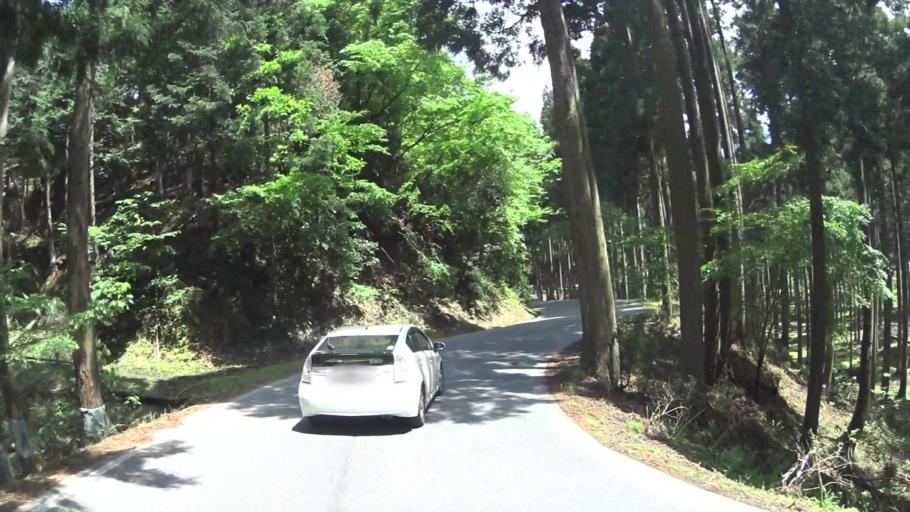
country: JP
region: Kyoto
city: Maizuru
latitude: 35.4430
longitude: 135.5093
